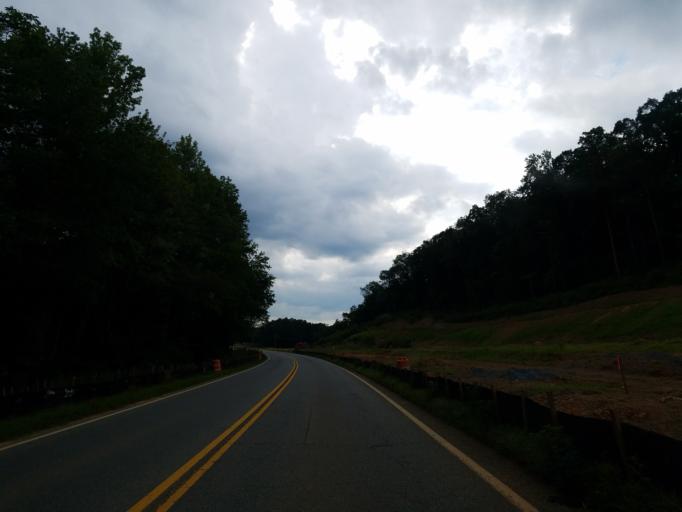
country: US
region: Georgia
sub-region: Floyd County
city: Shannon
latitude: 34.3692
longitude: -85.0177
